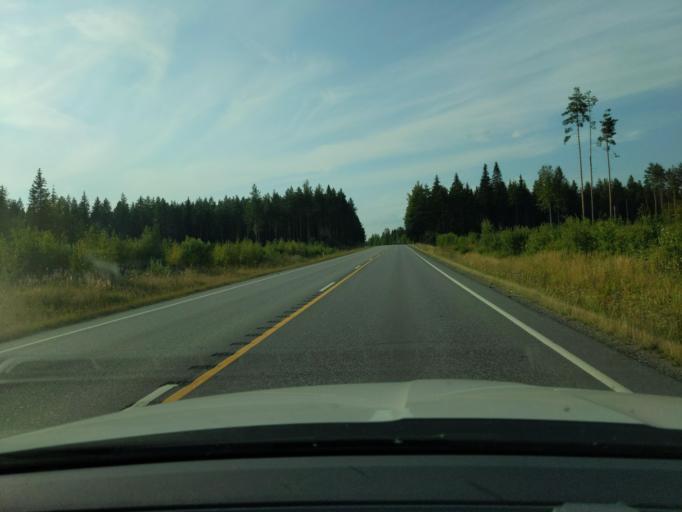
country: FI
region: Paijanne Tavastia
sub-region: Lahti
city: Padasjoki
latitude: 61.3307
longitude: 25.2707
